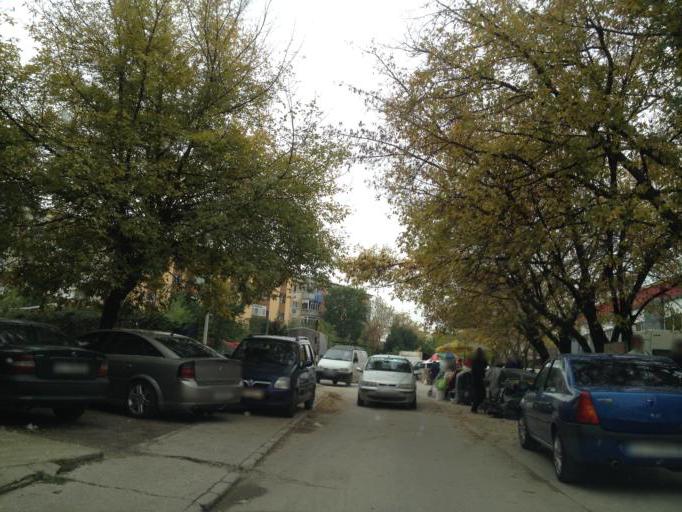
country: RO
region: Dolj
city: Craiova
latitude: 44.3003
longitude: 23.7972
